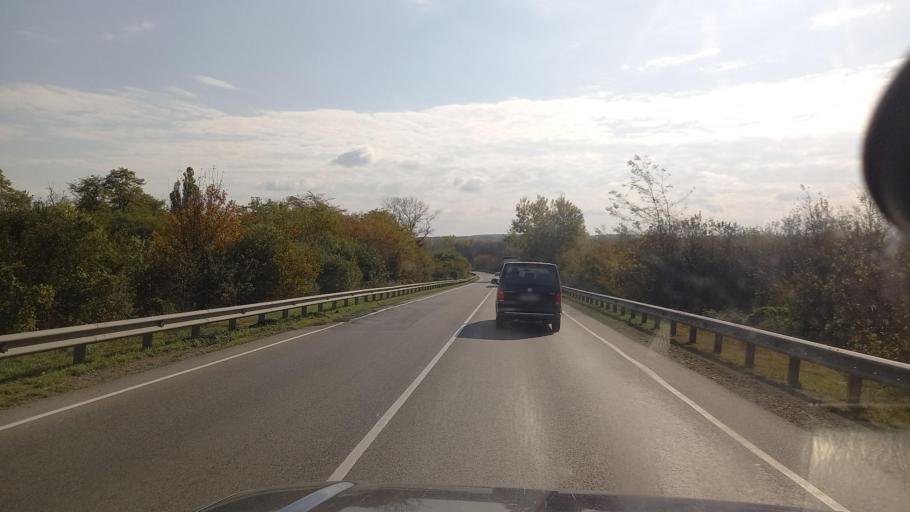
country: RU
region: Krasnodarskiy
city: Abinsk
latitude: 44.8461
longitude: 38.1498
